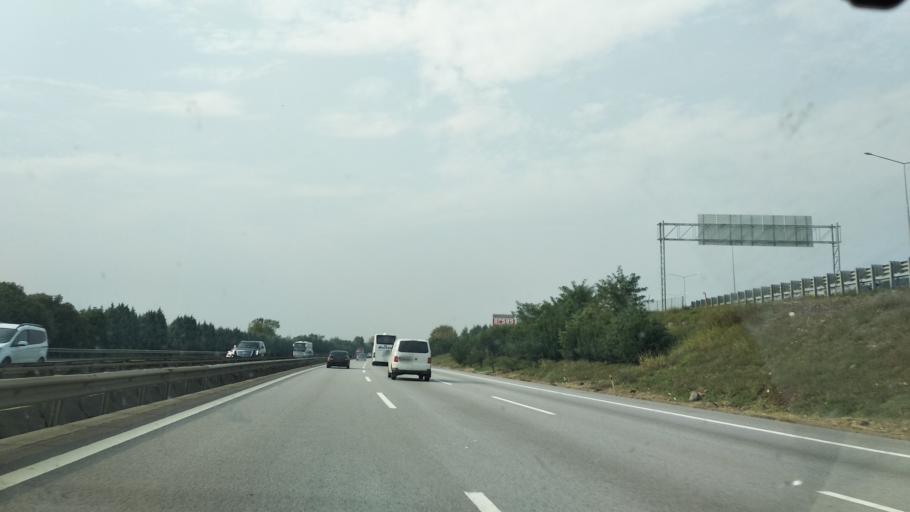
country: TR
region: Kocaeli
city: Derbent
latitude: 40.7331
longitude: 30.0547
